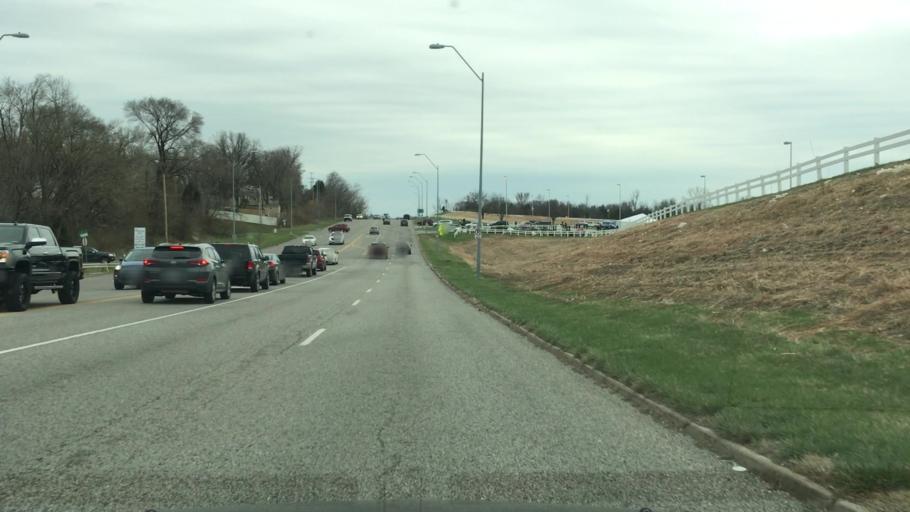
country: US
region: Missouri
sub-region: Jackson County
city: Raytown
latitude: 39.0458
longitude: -94.4758
